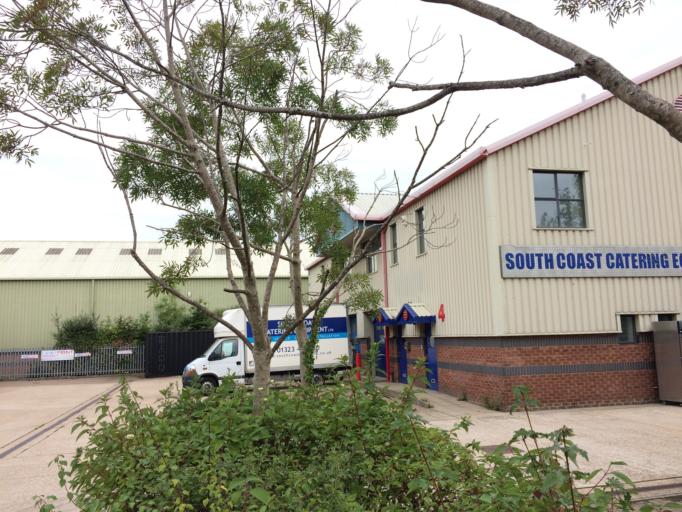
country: GB
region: England
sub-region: East Sussex
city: Hailsham
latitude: 50.8591
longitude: 0.2466
